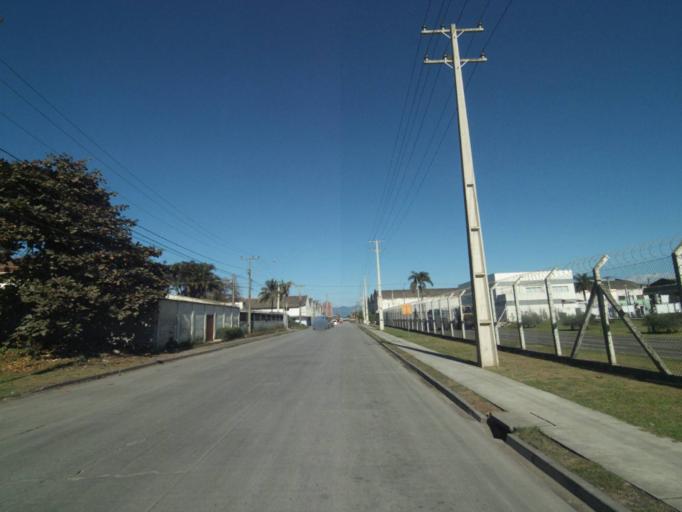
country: BR
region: Parana
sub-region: Paranagua
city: Paranagua
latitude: -25.5094
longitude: -48.5098
